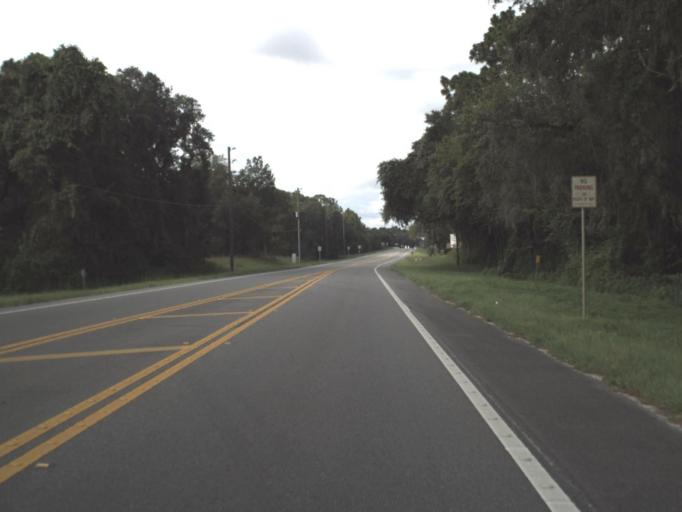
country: US
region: Florida
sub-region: Pasco County
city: Lacoochee
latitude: 28.4853
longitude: -82.1759
